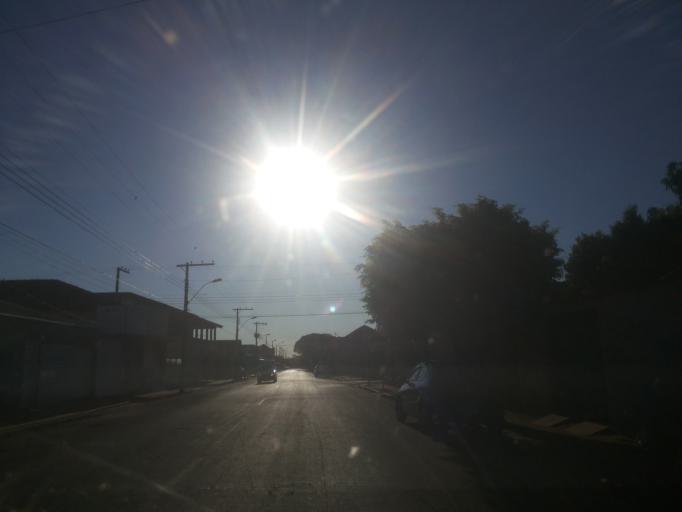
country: BR
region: Minas Gerais
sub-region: Centralina
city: Centralina
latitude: -18.7265
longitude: -49.2041
